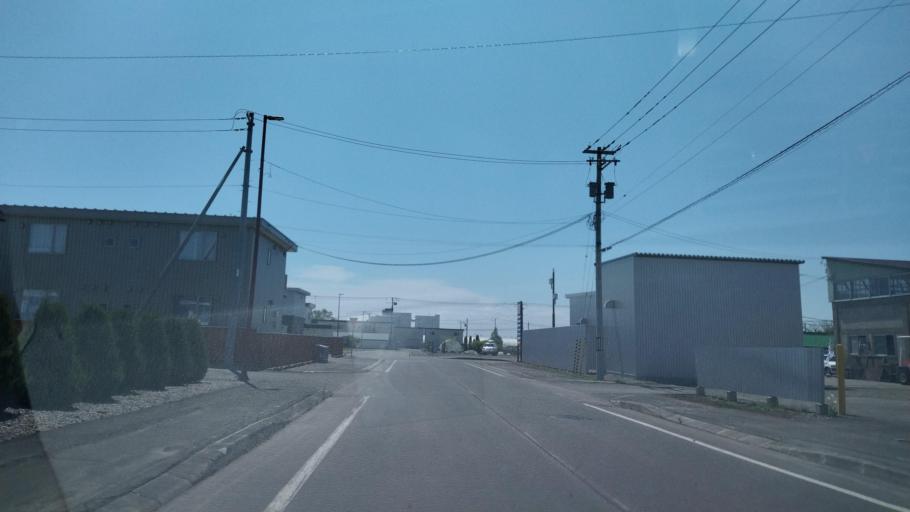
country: JP
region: Hokkaido
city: Otofuke
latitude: 43.1697
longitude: 143.2519
